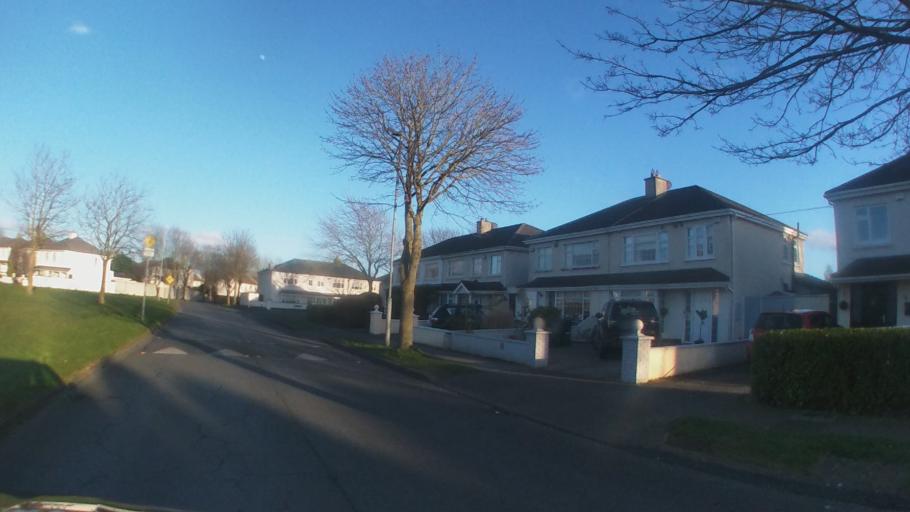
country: IE
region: Leinster
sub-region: Fingal County
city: Blanchardstown
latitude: 53.3772
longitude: -6.3855
